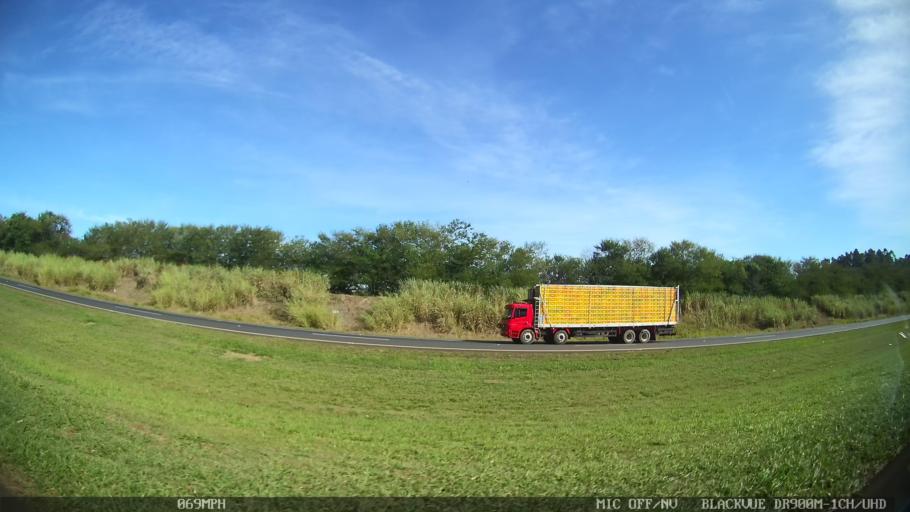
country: BR
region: Sao Paulo
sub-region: Leme
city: Leme
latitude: -22.2339
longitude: -47.3910
